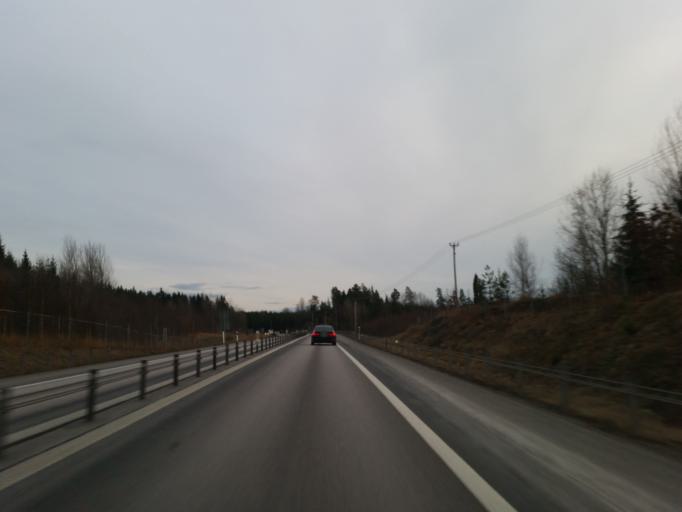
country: SE
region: OEstergoetland
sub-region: Valdemarsviks Kommun
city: Gusum
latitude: 58.2707
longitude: 16.5177
